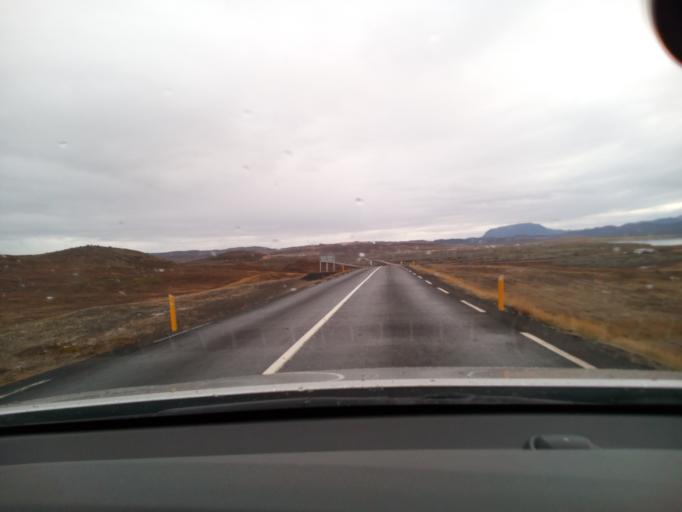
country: IS
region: Northeast
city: Laugar
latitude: 65.6602
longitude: -16.9728
